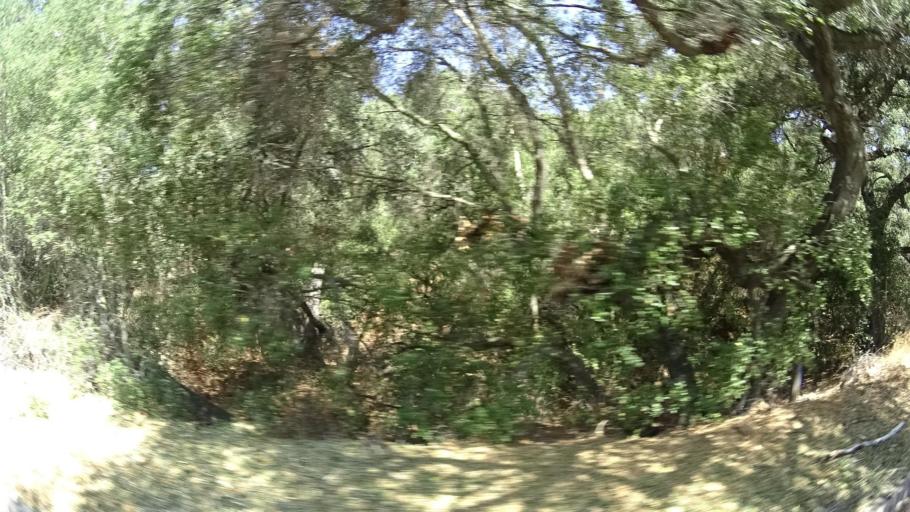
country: US
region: California
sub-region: San Diego County
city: Fallbrook
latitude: 33.4119
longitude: -117.2879
